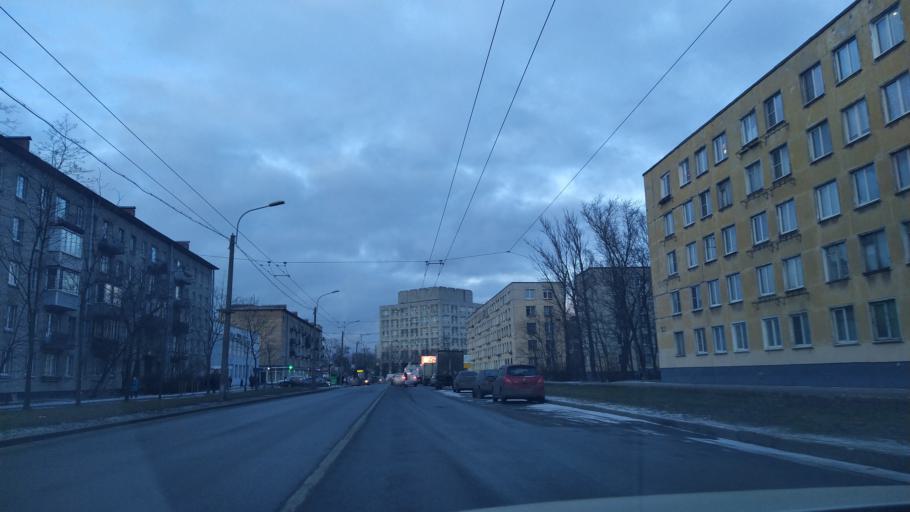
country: RU
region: St.-Petersburg
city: Dachnoye
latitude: 59.8550
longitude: 30.2564
